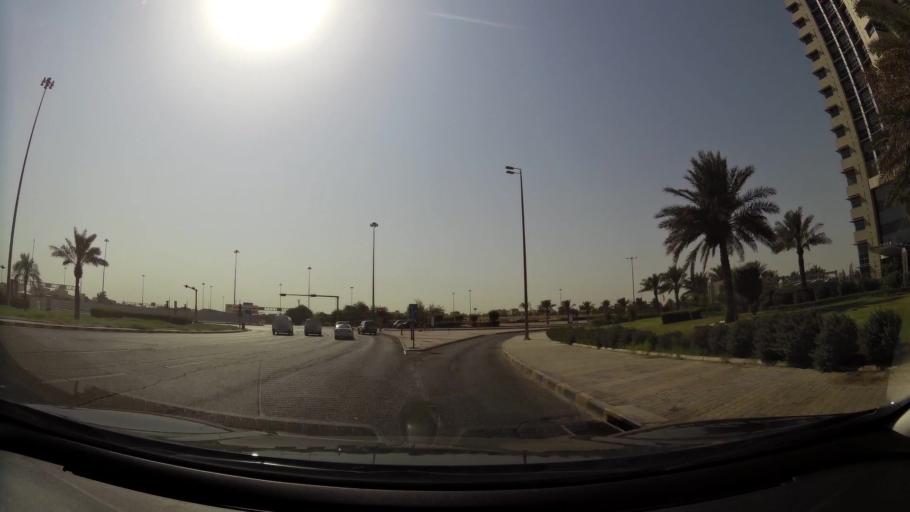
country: KW
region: Al Asimah
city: Kuwait City
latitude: 29.3636
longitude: 47.9847
